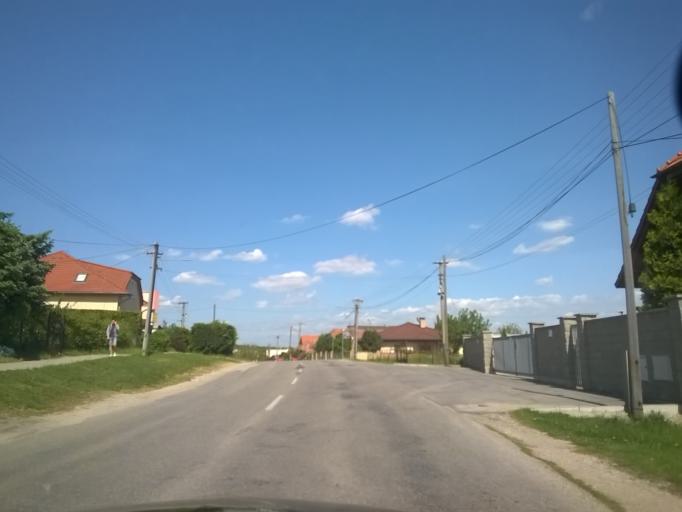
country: SK
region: Nitriansky
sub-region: Okres Nitra
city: Nitra
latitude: 48.3297
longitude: 18.1212
